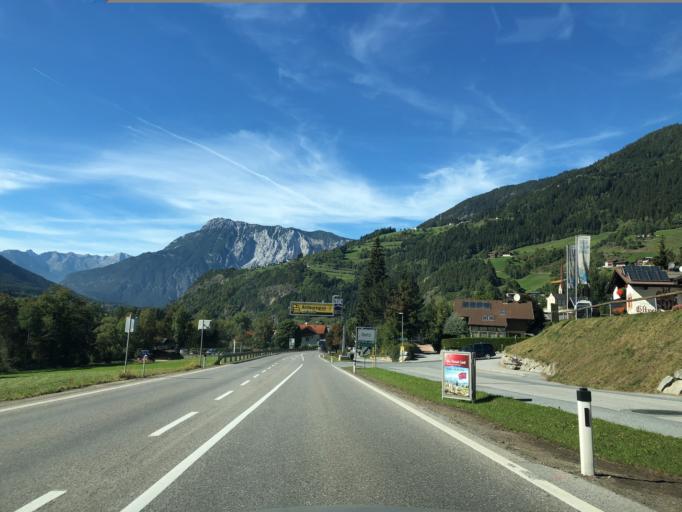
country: AT
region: Tyrol
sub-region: Politischer Bezirk Imst
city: Oetz
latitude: 47.1987
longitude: 10.9023
